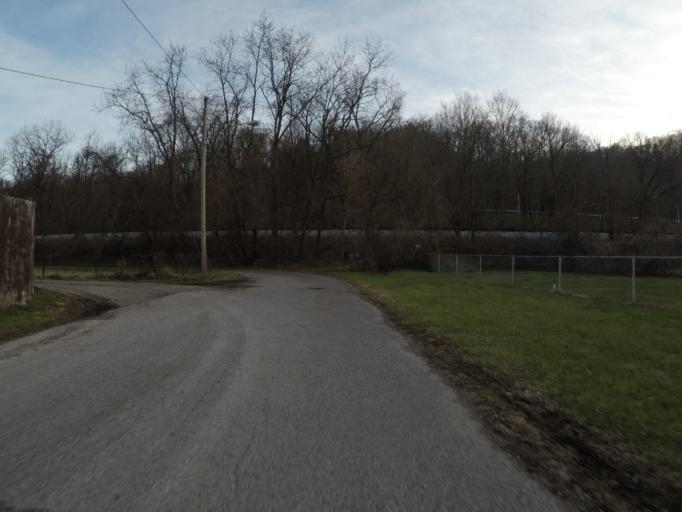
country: US
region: Ohio
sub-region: Lawrence County
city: Burlington
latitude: 38.3985
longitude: -82.5064
